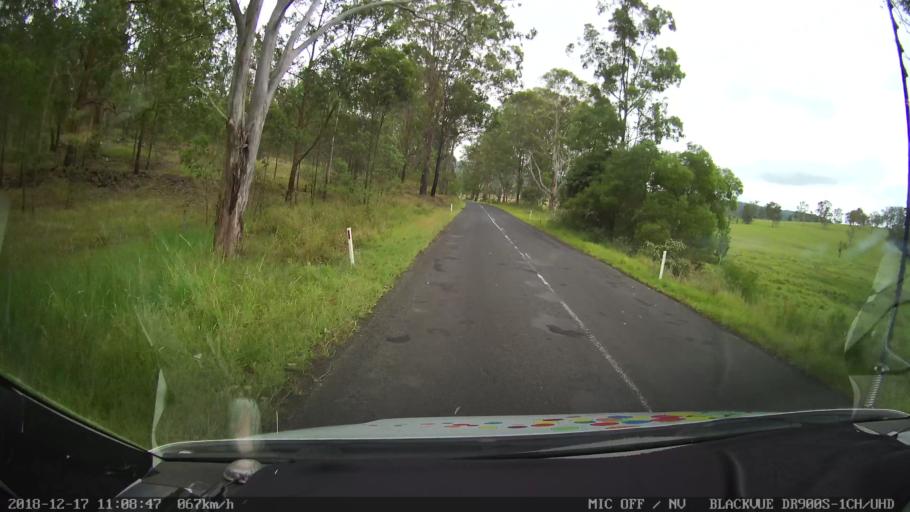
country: AU
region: New South Wales
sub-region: Kyogle
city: Kyogle
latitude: -28.7604
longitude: 152.6552
